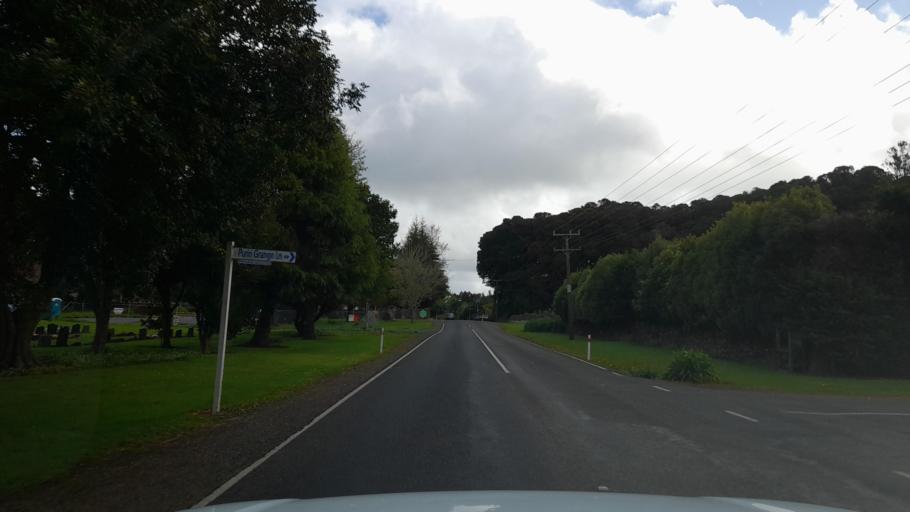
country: NZ
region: Northland
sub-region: Whangarei
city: Maungatapere
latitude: -35.7449
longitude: 174.2567
